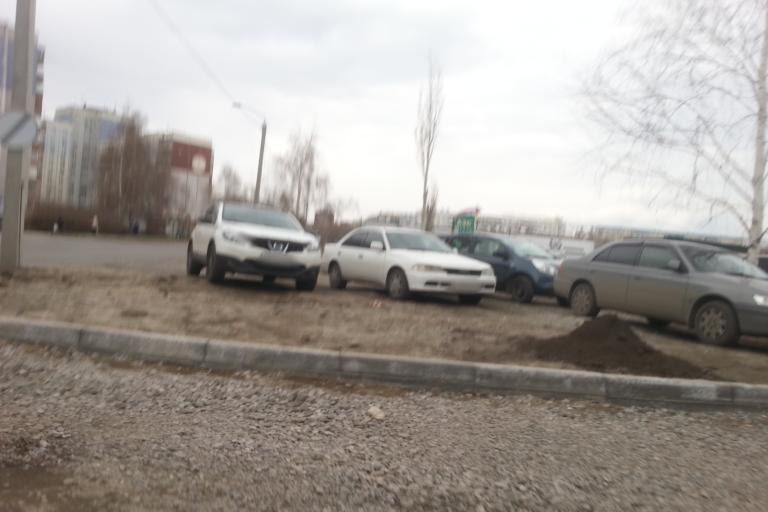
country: RU
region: Altai Krai
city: Novosilikatnyy
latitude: 53.3409
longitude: 83.6788
